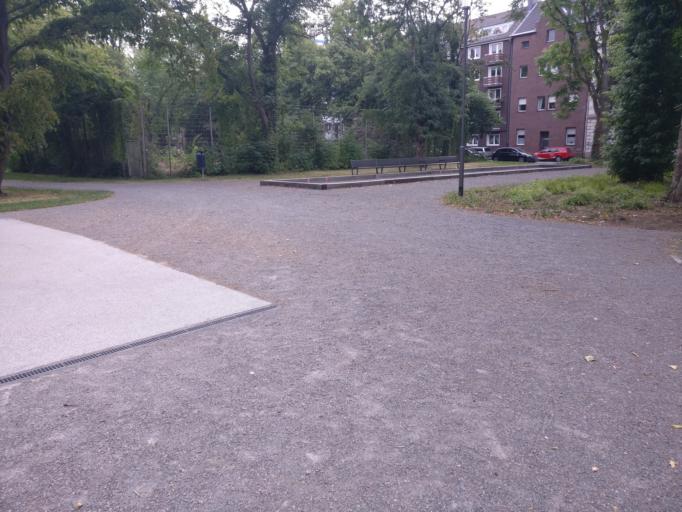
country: DE
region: North Rhine-Westphalia
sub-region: Regierungsbezirk Dusseldorf
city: Duisburg
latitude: 51.4282
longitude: 6.7672
